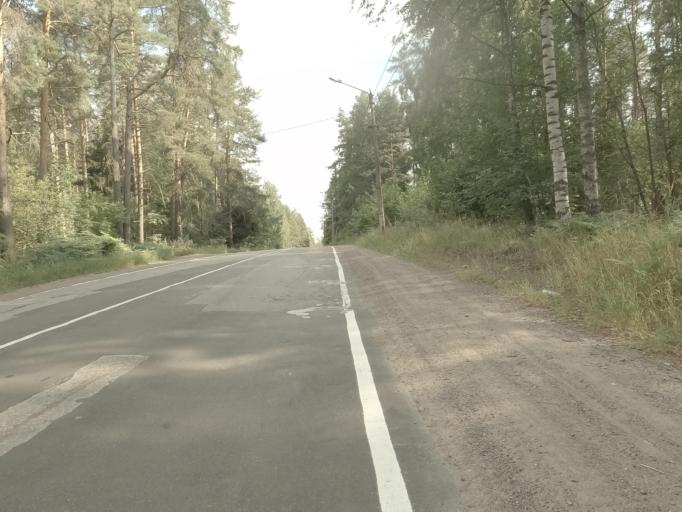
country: RU
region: Leningrad
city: Kamennogorsk
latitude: 60.9371
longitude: 29.1573
